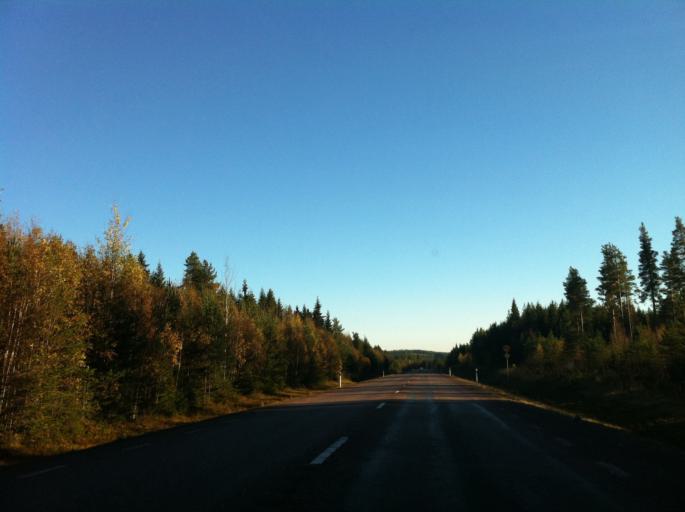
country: SE
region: Dalarna
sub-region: Rattviks Kommun
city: Raettvik
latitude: 60.8289
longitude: 15.2429
